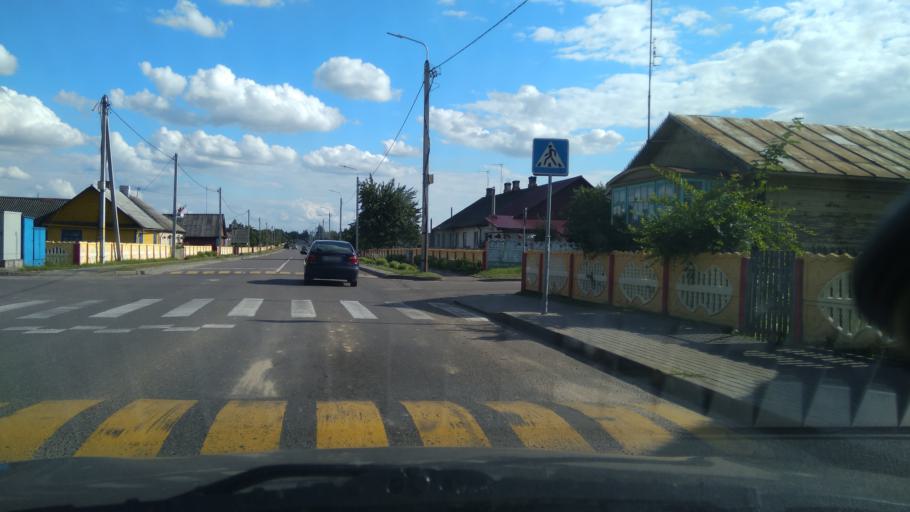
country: BY
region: Grodnenskaya
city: Masty
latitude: 53.4015
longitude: 24.5346
